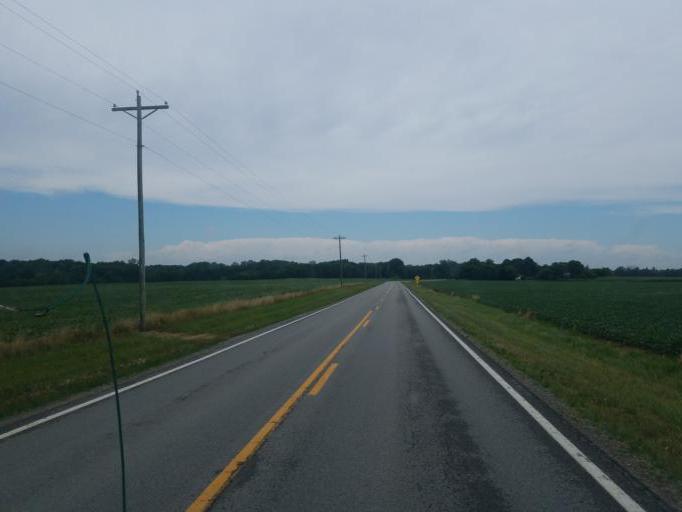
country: US
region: Ohio
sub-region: Williams County
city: Edgerton
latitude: 41.3826
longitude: -84.7900
